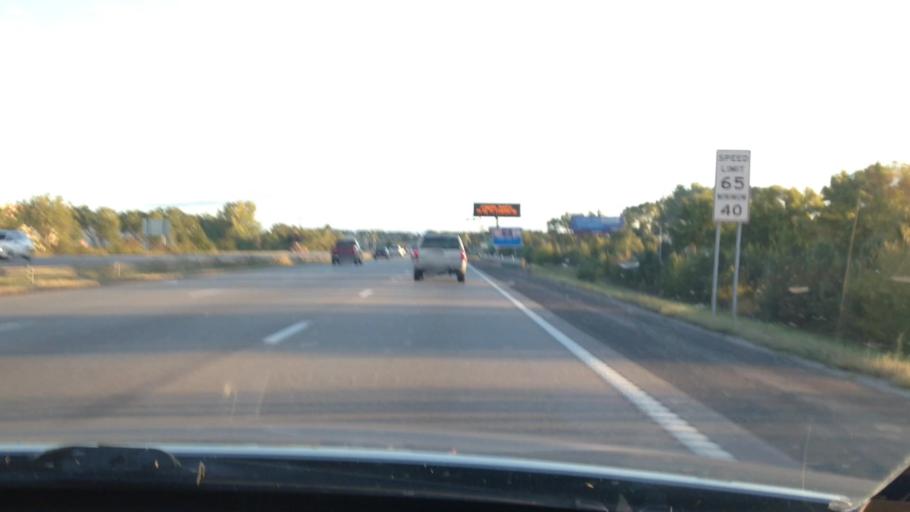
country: US
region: Missouri
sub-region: Jackson County
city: Sugar Creek
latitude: 39.1397
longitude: -94.4989
